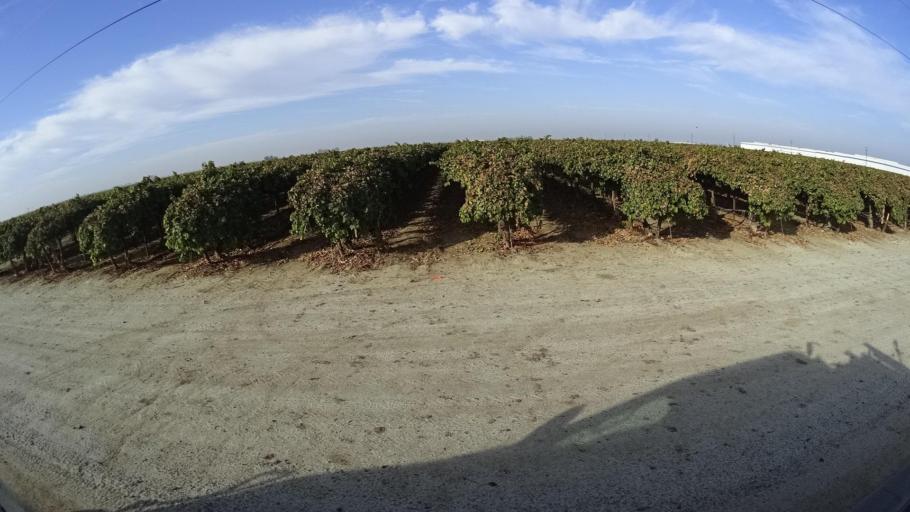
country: US
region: California
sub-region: Kern County
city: McFarland
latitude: 35.7013
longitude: -119.2049
